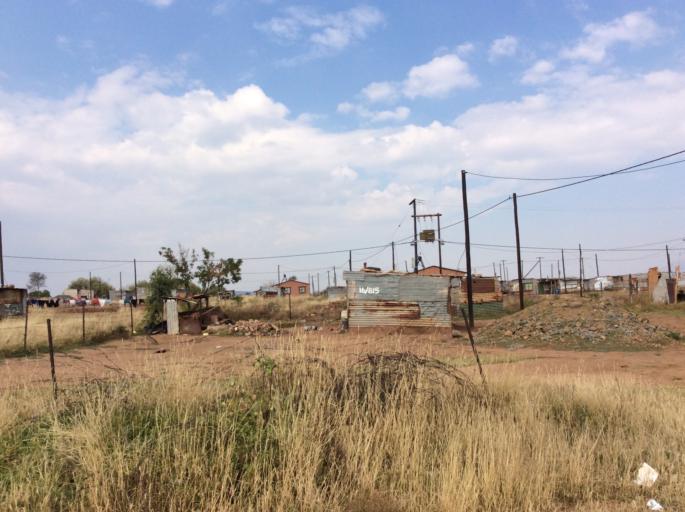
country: LS
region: Mafeteng
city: Mafeteng
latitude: -29.9860
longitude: 27.0017
